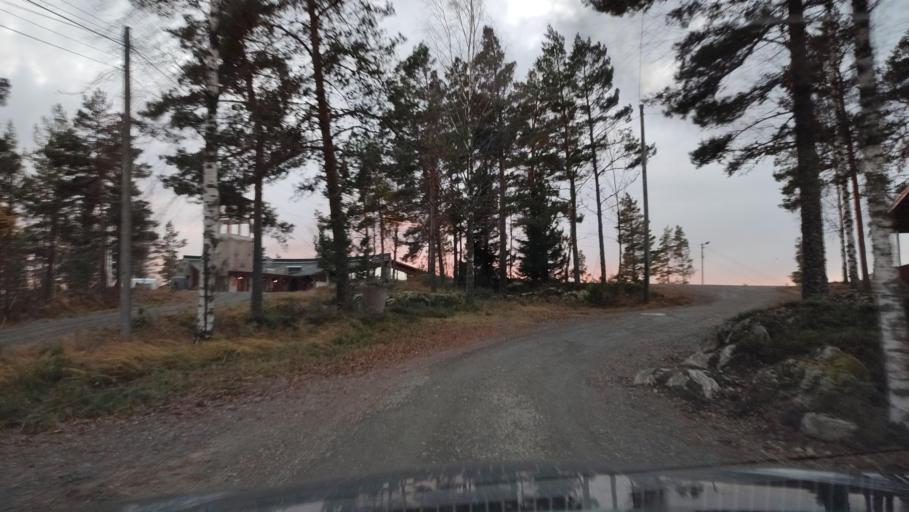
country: FI
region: Southern Ostrobothnia
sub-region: Suupohja
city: Karijoki
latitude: 62.2822
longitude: 21.6281
